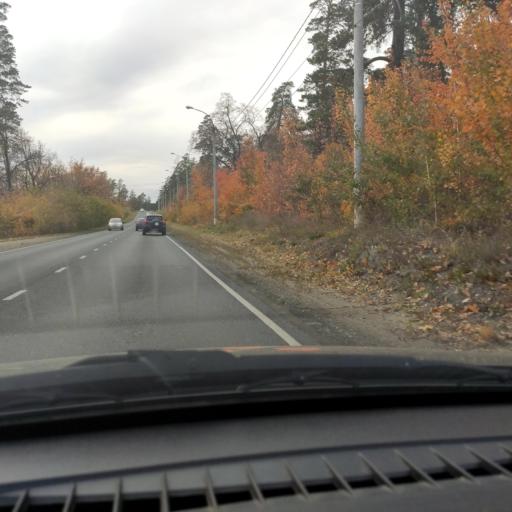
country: RU
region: Samara
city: Tol'yatti
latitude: 53.4733
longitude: 49.3923
